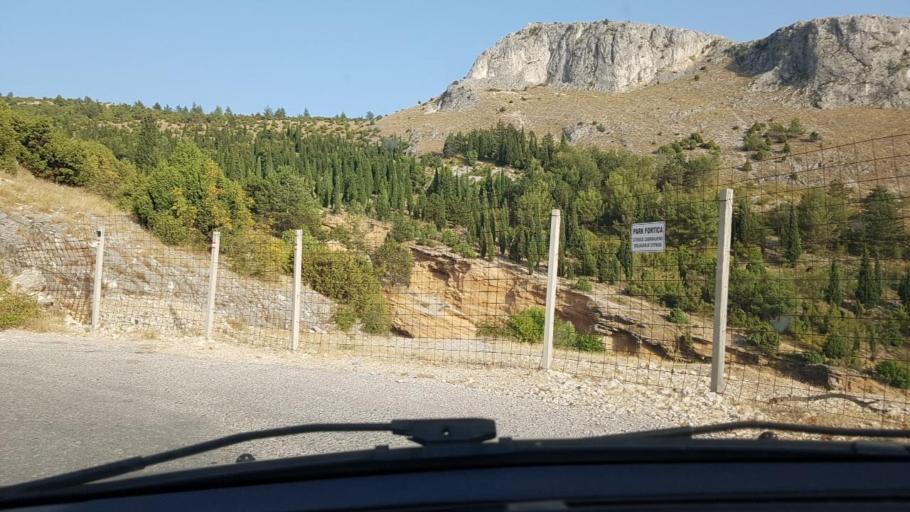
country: BA
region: Federation of Bosnia and Herzegovina
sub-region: Hercegovacko-Bosanski Kanton
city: Mostar
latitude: 43.3469
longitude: 17.8268
